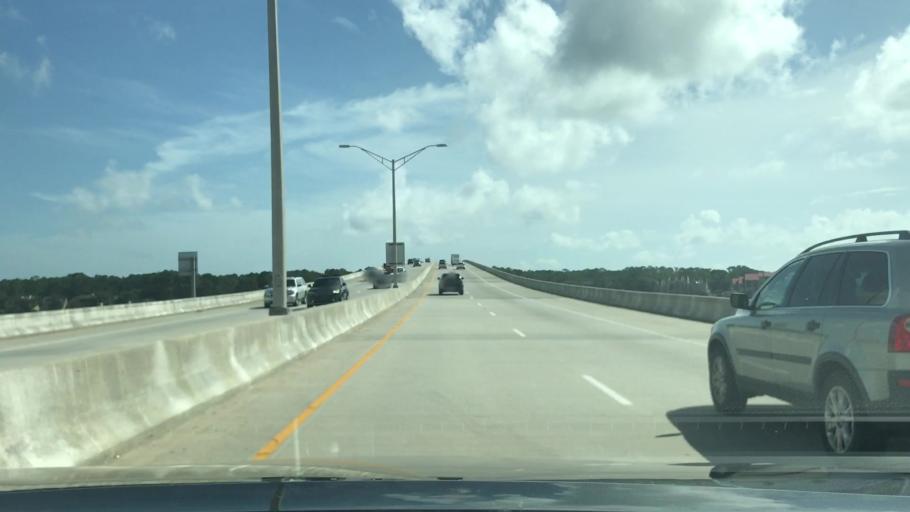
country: US
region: South Carolina
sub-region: Beaufort County
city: Hilton Head Island
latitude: 32.1820
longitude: -80.7667
